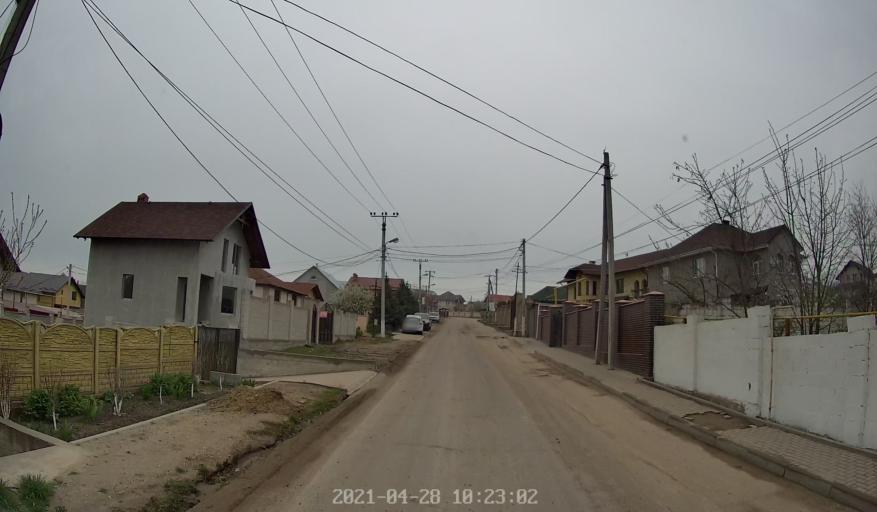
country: MD
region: Chisinau
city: Chisinau
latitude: 46.9942
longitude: 28.9350
